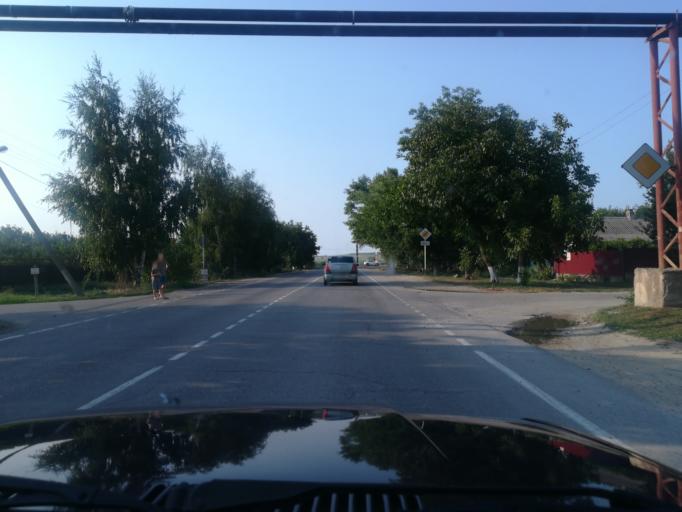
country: RU
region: Krasnodarskiy
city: Yurovka
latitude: 45.1170
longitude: 37.4220
